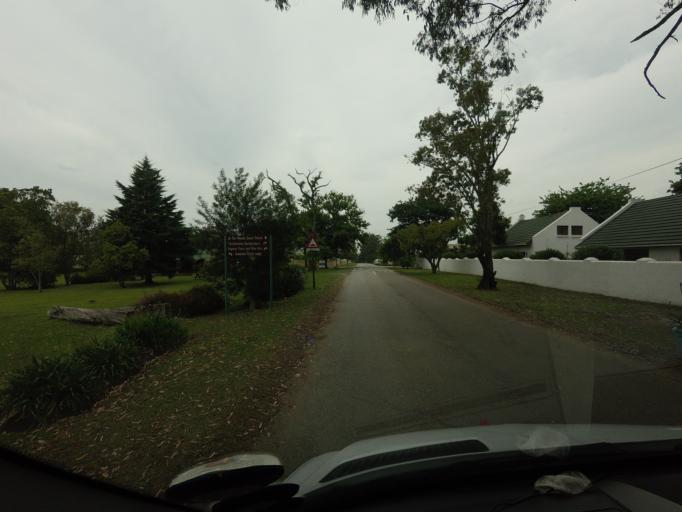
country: ZA
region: Eastern Cape
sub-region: Cacadu District Municipality
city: Kareedouw
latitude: -33.9714
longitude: 23.8871
